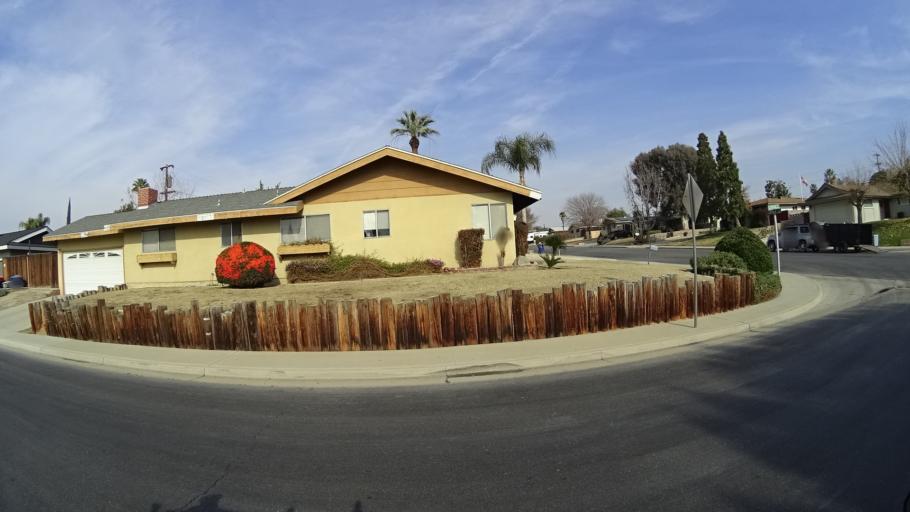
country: US
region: California
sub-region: Kern County
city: Oildale
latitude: 35.3981
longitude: -118.9618
